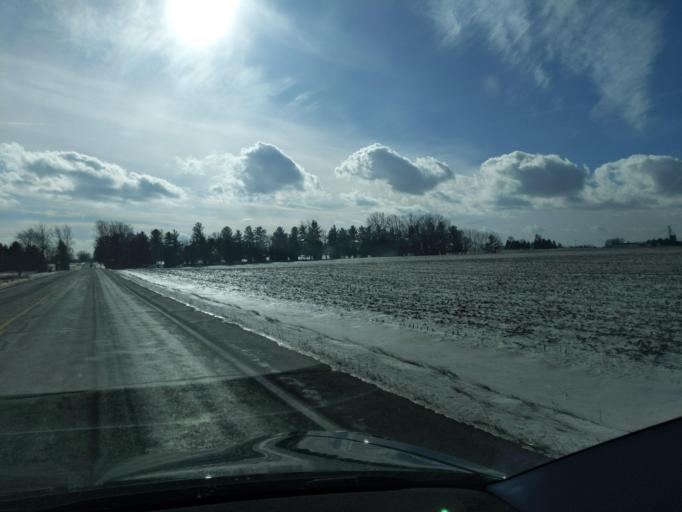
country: US
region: Michigan
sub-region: Ingham County
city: Williamston
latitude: 42.6058
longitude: -84.2795
